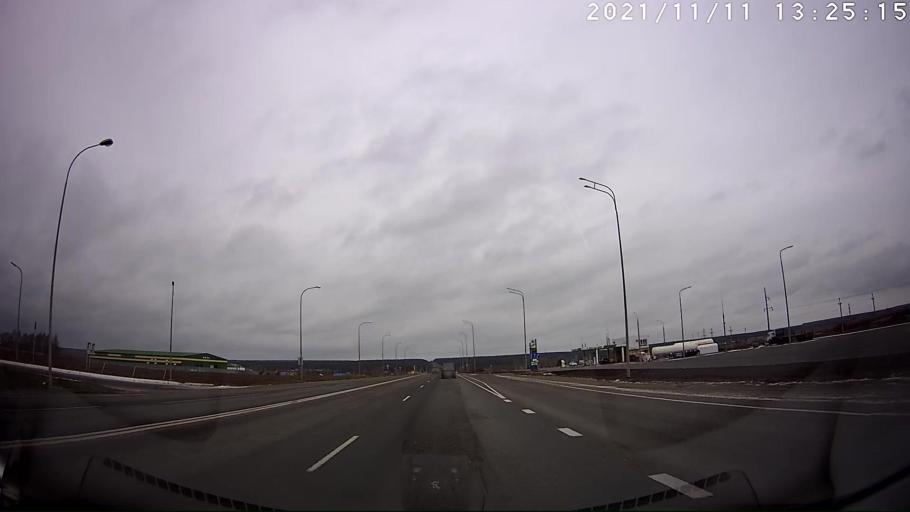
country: RU
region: Chuvashia
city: Komsomol'skoye
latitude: 55.2562
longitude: 47.5600
